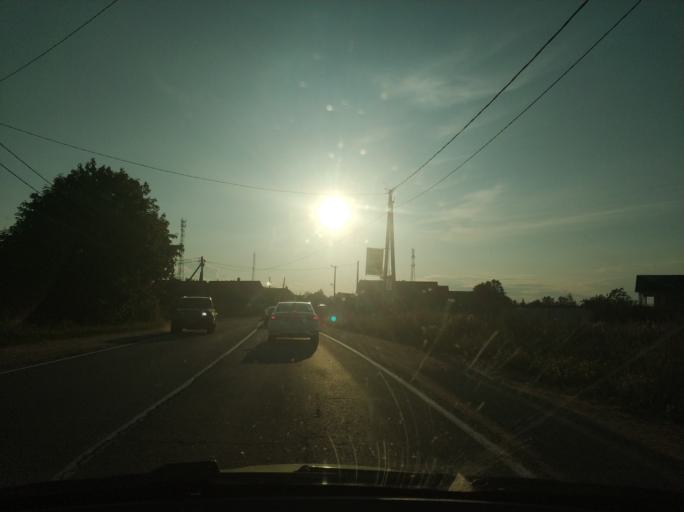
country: RU
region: Leningrad
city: Borisova Griva
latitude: 60.0852
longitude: 31.0262
